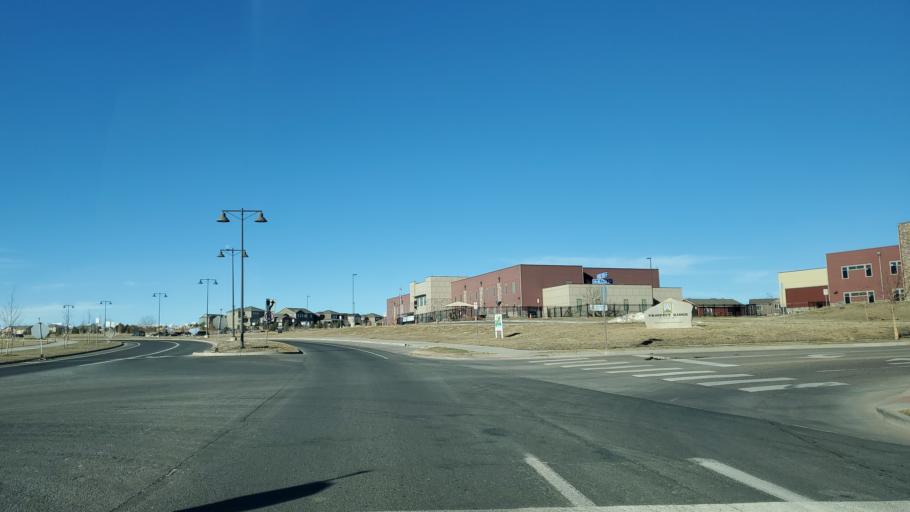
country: US
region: Colorado
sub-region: Boulder County
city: Erie
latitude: 39.9934
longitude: -105.0161
